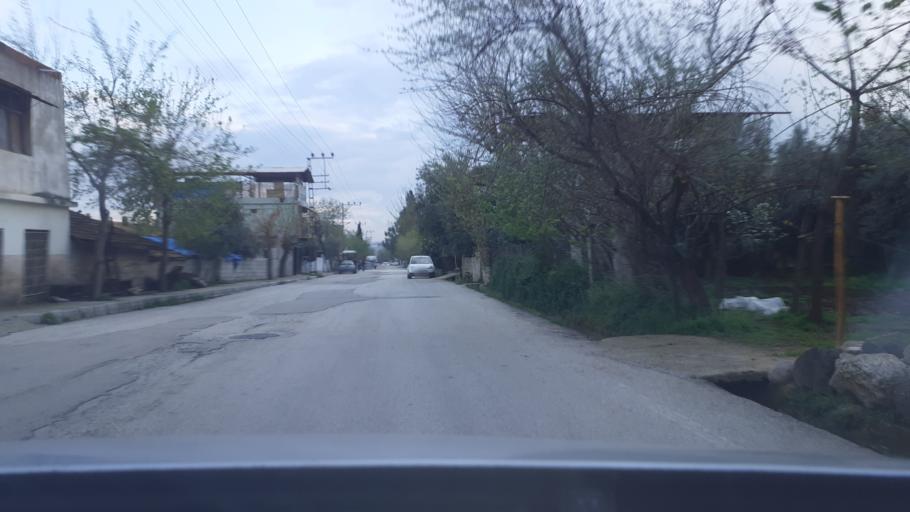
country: TR
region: Hatay
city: Kirikhan
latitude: 36.4864
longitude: 36.3504
